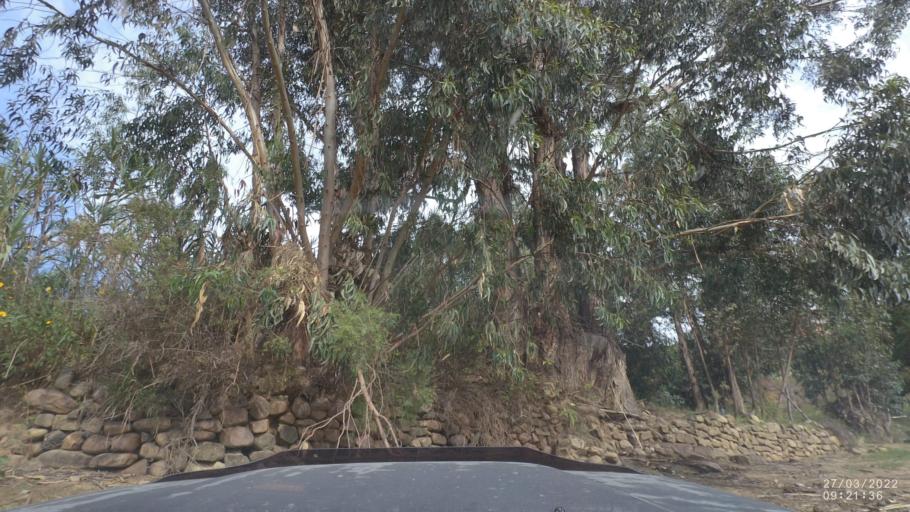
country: BO
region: Cochabamba
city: Cliza
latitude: -17.7307
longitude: -65.8752
